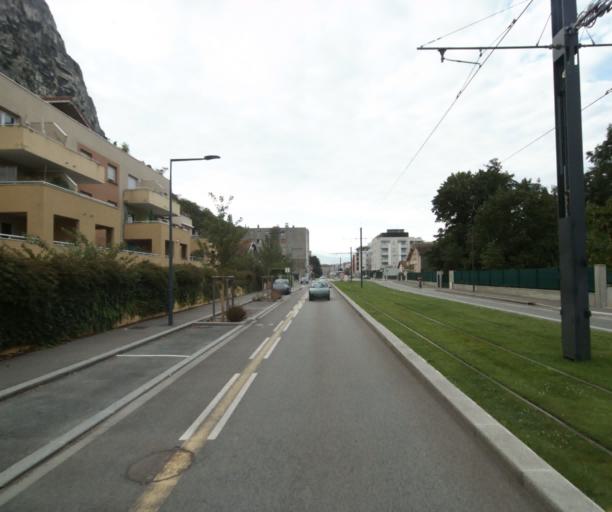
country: FR
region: Rhone-Alpes
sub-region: Departement de l'Isere
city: Saint-Egreve
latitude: 45.2187
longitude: 5.6928
